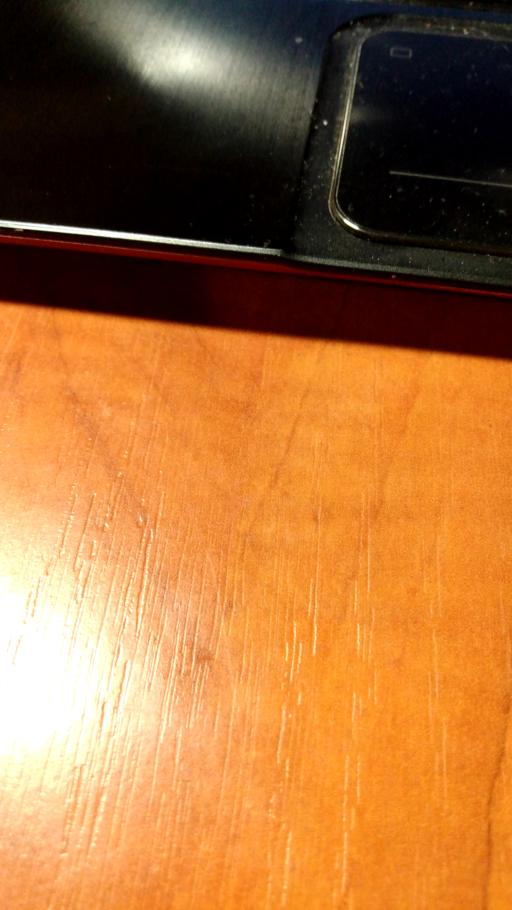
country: RU
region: Novgorod
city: Marevo
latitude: 57.3338
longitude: 32.0179
